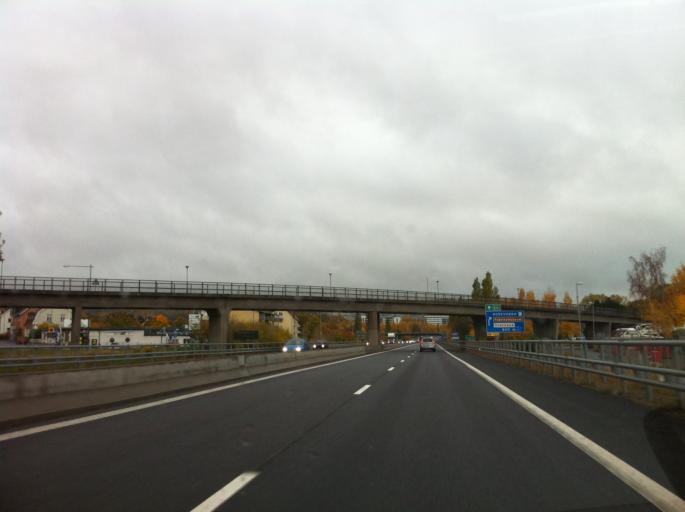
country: SE
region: Joenkoeping
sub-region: Jonkopings Kommun
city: Huskvarna
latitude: 57.7972
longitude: 14.2688
